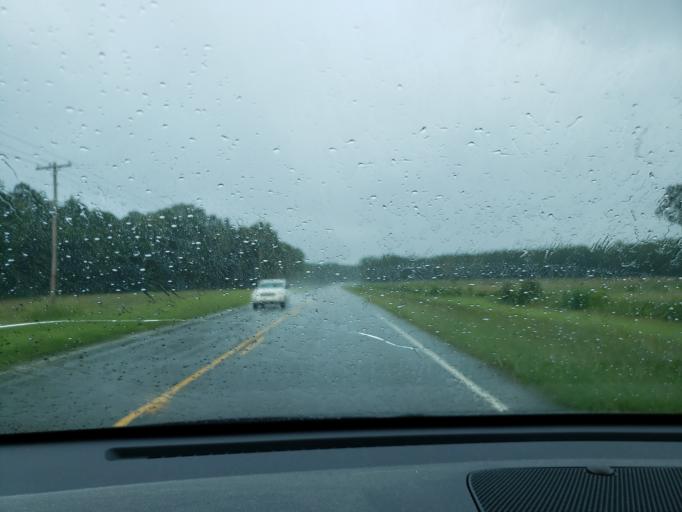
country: US
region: North Carolina
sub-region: Bladen County
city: Elizabethtown
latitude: 34.5197
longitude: -78.6522
